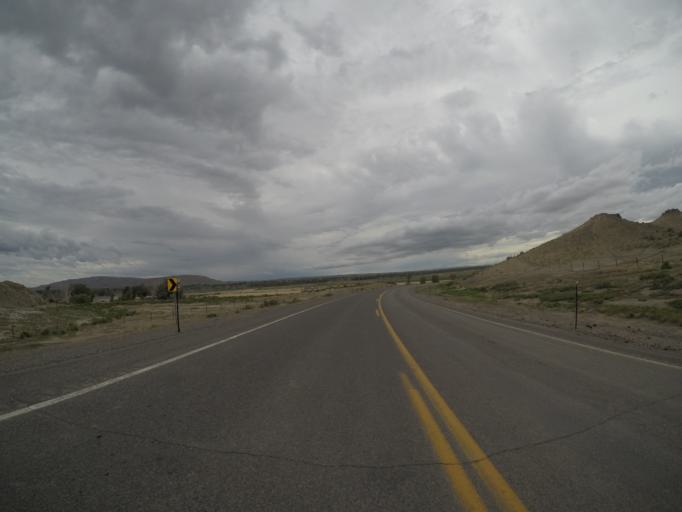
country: US
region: Wyoming
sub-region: Big Horn County
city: Lovell
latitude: 44.8795
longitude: -108.2902
